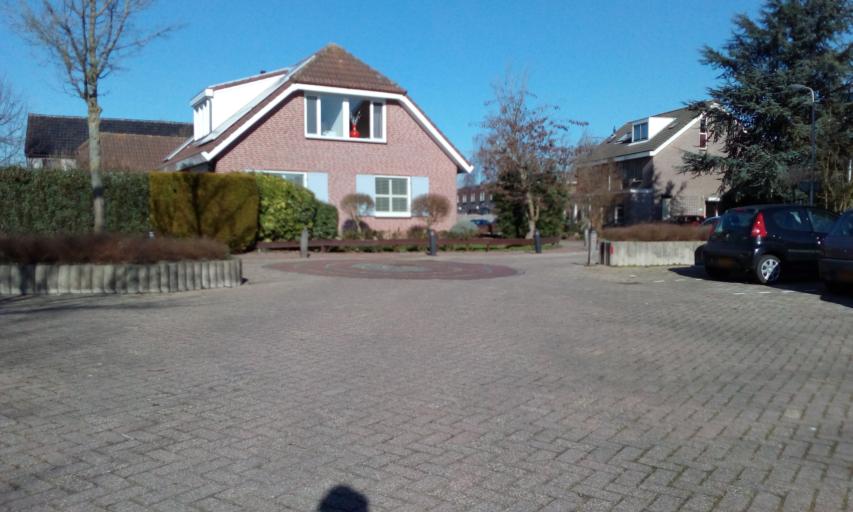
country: NL
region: South Holland
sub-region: Gemeente Lansingerland
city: Bleiswijk
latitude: 52.0062
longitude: 4.5787
